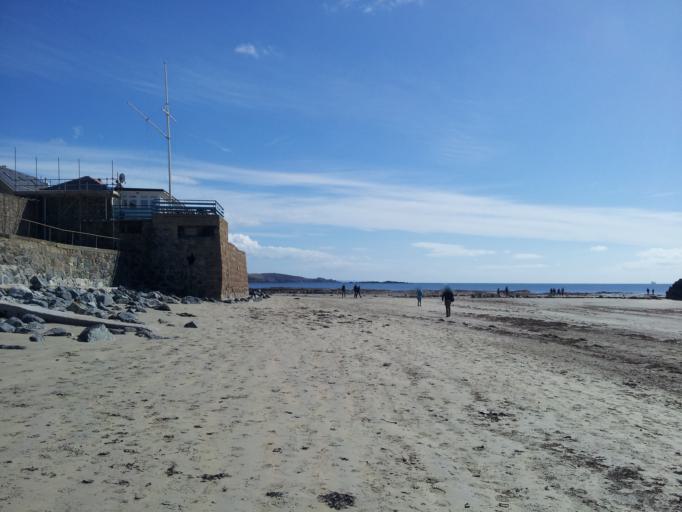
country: GB
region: England
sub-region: Cornwall
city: Marazion
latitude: 50.1236
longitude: -5.4759
